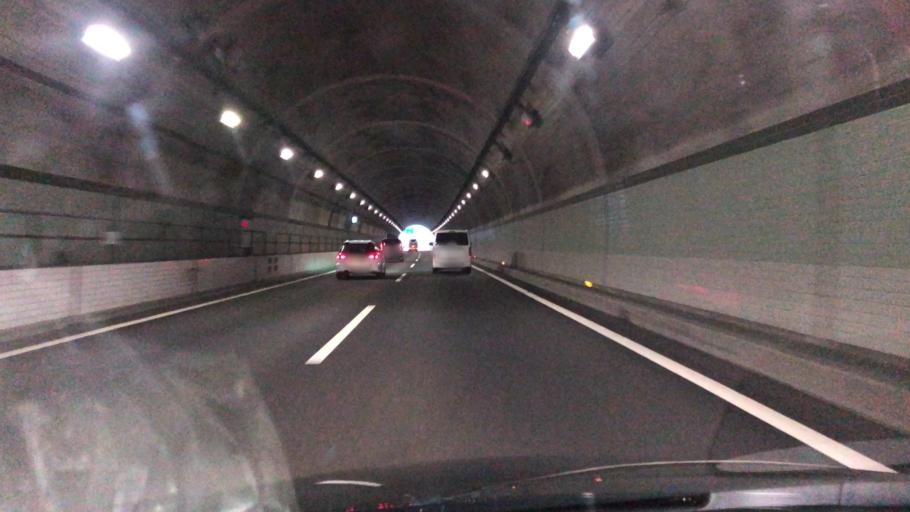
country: JP
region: Tokyo
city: Itsukaichi
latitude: 35.6709
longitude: 139.2508
